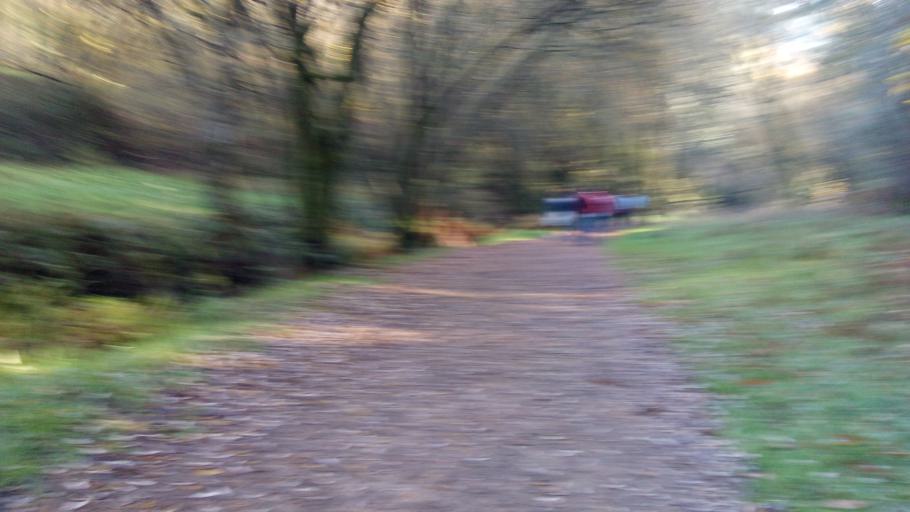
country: ES
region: Galicia
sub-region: Provincia de Pontevedra
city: Meis
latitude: 42.4858
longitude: -8.7462
